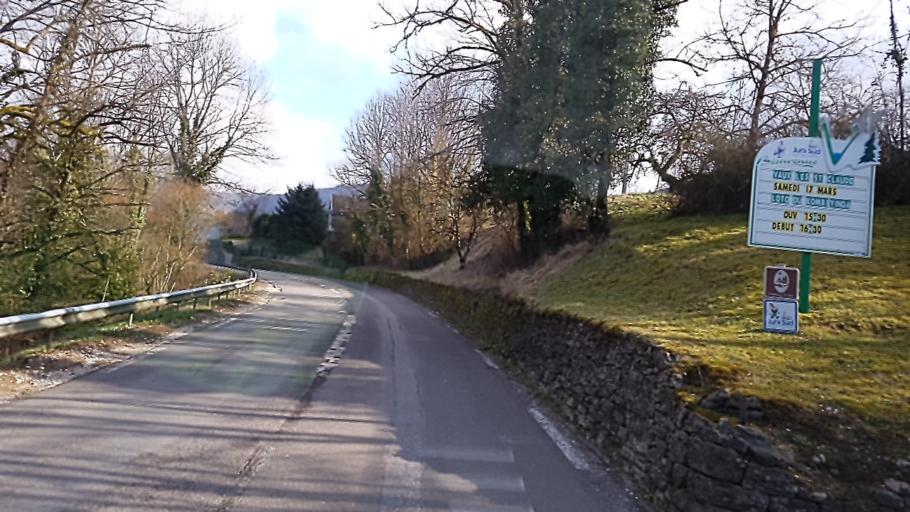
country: FR
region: Franche-Comte
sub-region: Departement du Jura
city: Lavans-les-Saint-Claude
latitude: 46.3611
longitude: 5.7310
